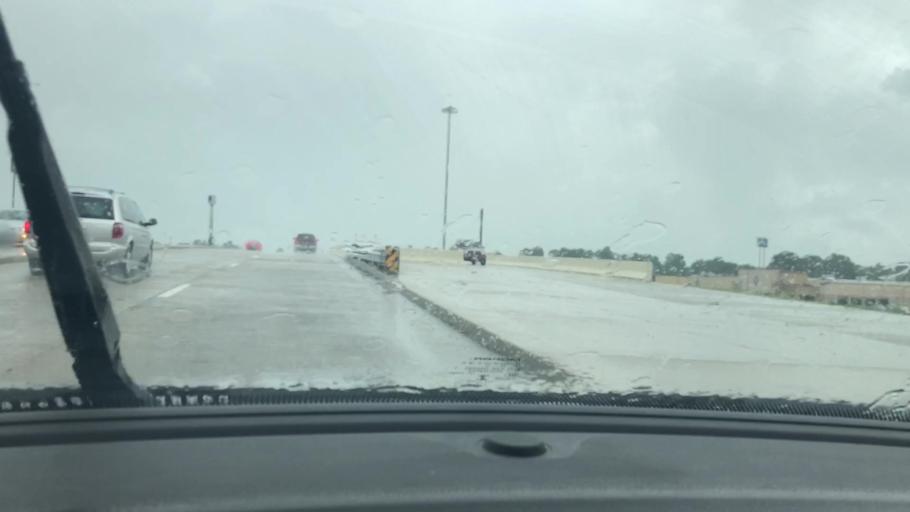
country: US
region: Texas
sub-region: Bowie County
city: Wake Village
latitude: 33.4557
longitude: -94.0860
